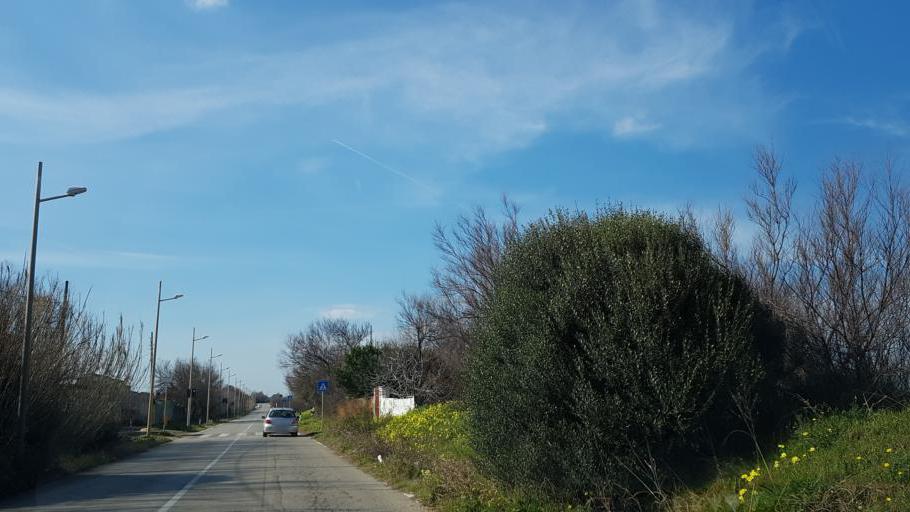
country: IT
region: Apulia
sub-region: Provincia di Brindisi
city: Brindisi
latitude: 40.6843
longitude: 17.8790
